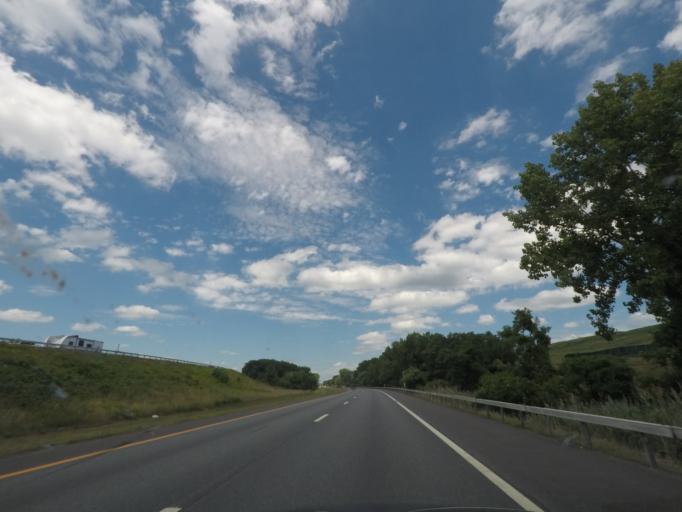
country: US
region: New York
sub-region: Albany County
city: McKownville
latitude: 42.7044
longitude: -73.8518
